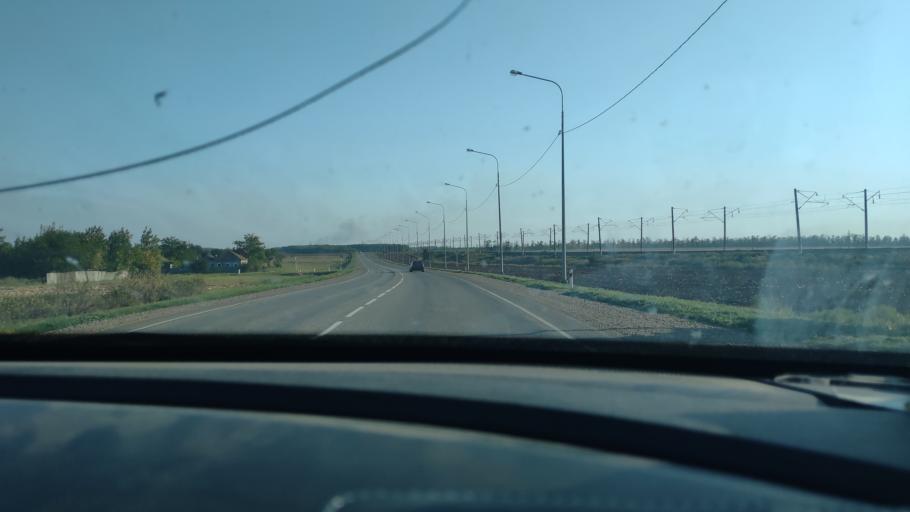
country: RU
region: Krasnodarskiy
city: Novominskaya
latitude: 46.3168
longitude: 38.9307
